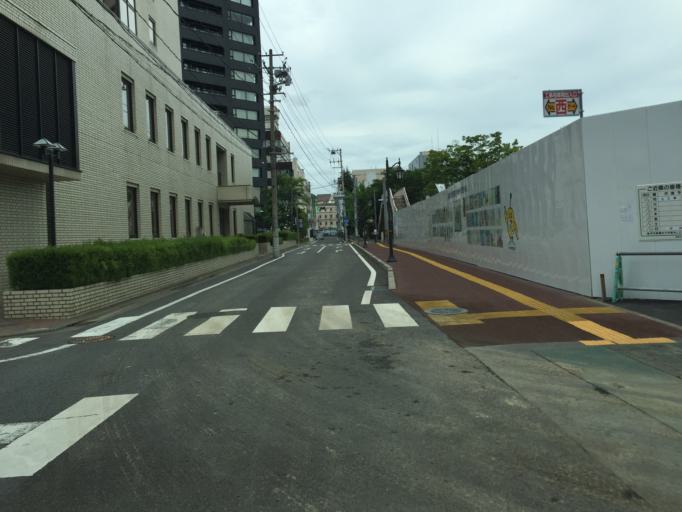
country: JP
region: Fukushima
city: Fukushima-shi
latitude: 37.7504
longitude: 140.4661
